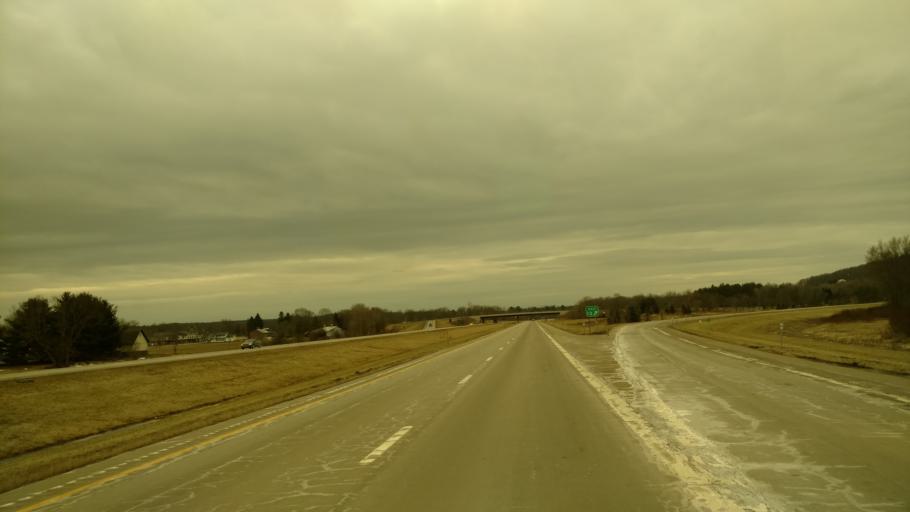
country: US
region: New York
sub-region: Chautauqua County
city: Falconer
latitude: 42.1335
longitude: -79.1849
